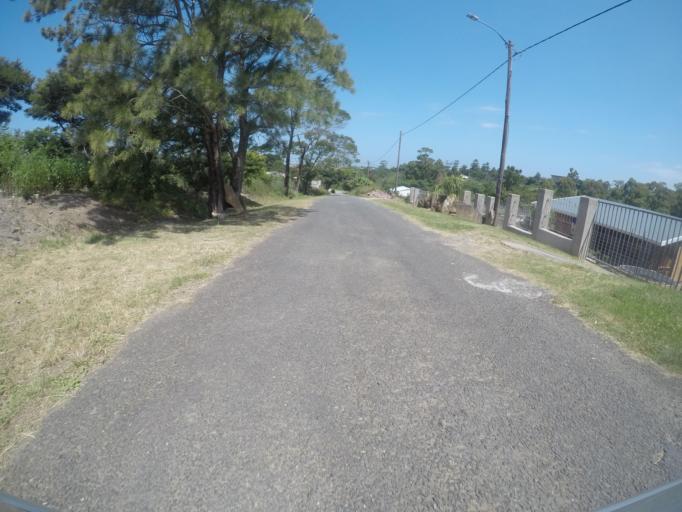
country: ZA
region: Eastern Cape
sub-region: Buffalo City Metropolitan Municipality
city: East London
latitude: -32.9684
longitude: 27.8544
